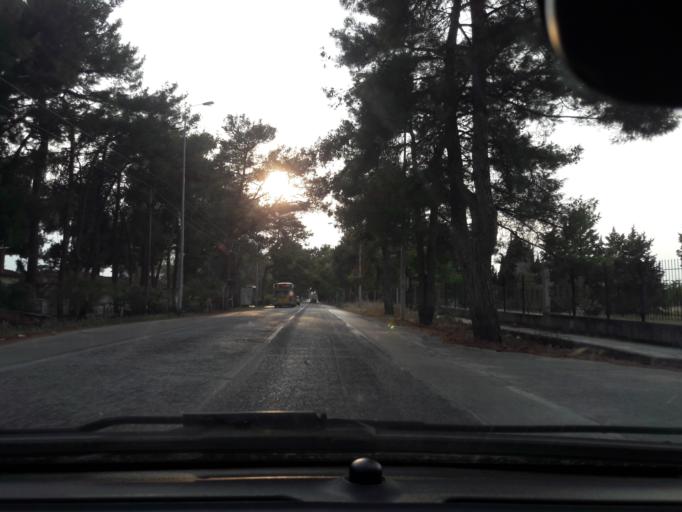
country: GR
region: Central Macedonia
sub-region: Nomos Thessalonikis
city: Thermi
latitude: 40.5389
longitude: 23.0018
